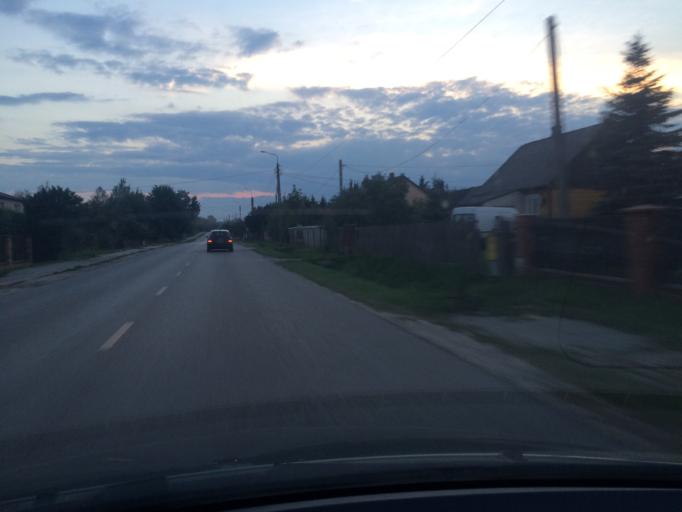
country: PL
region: Swietokrzyskie
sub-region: Powiat skarzyski
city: Suchedniow
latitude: 51.0456
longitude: 20.8754
